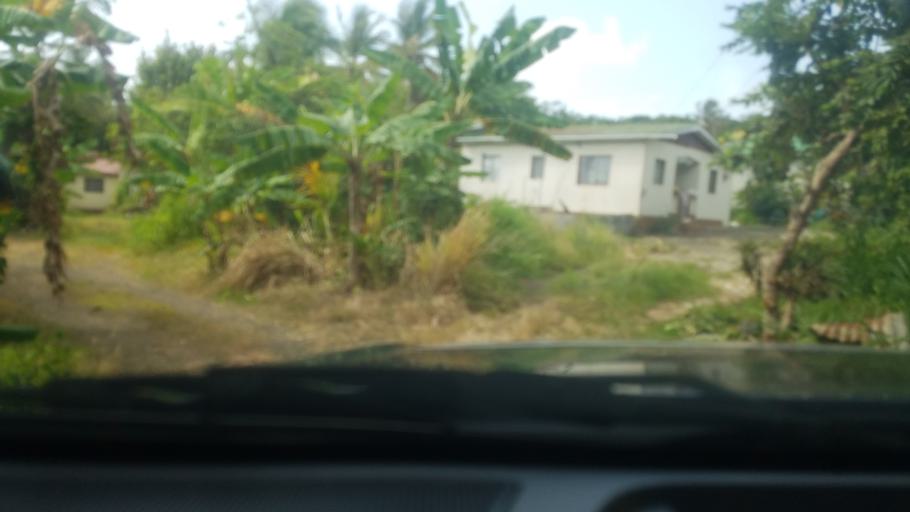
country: LC
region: Micoud Quarter
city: Micoud
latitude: 13.7978
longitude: -60.9261
